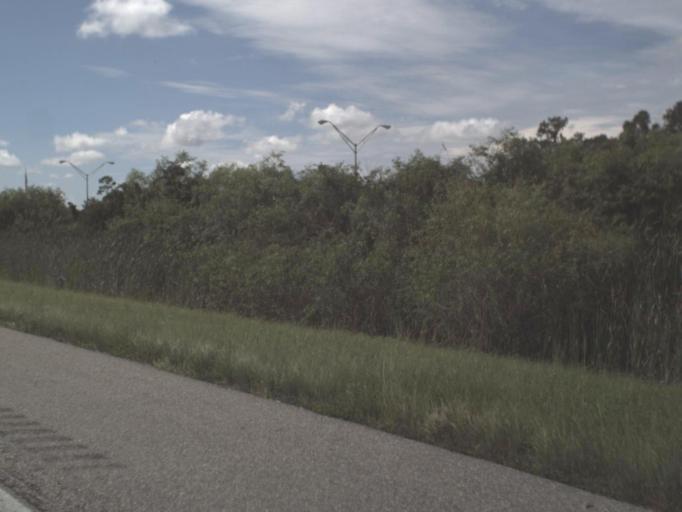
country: US
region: Florida
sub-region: Charlotte County
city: Harbour Heights
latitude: 27.0274
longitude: -82.0530
